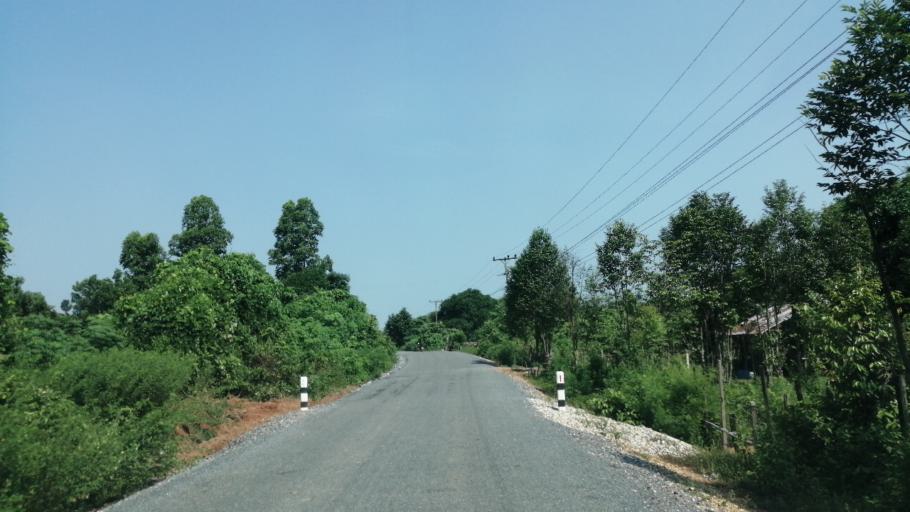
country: LA
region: Bolikhamxai
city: Bolikhan
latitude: 18.4522
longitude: 103.8063
